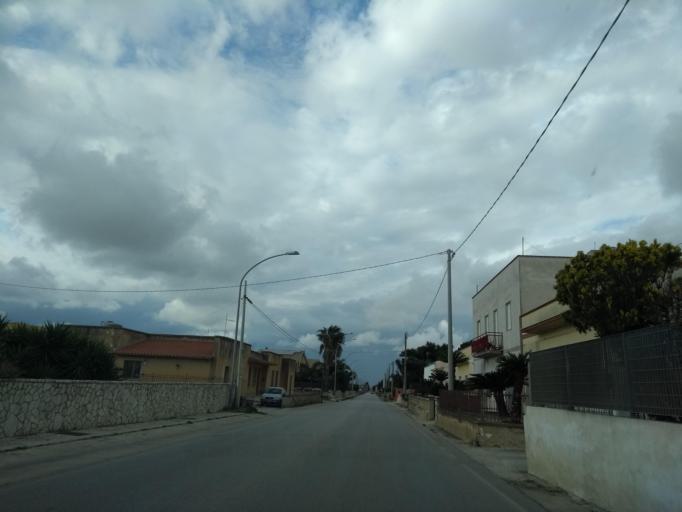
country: IT
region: Sicily
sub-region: Trapani
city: Marausa
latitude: 37.9566
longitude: 12.5166
